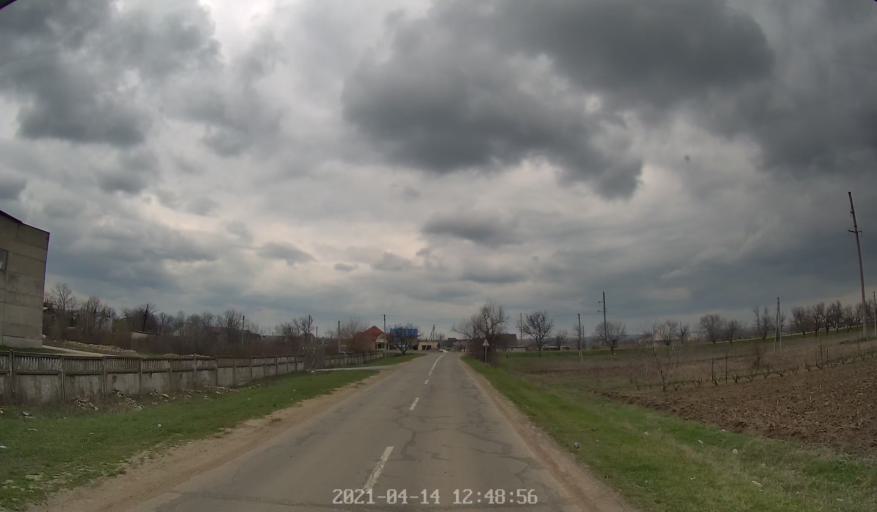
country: MD
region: Criuleni
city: Criuleni
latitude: 47.1547
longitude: 29.1516
